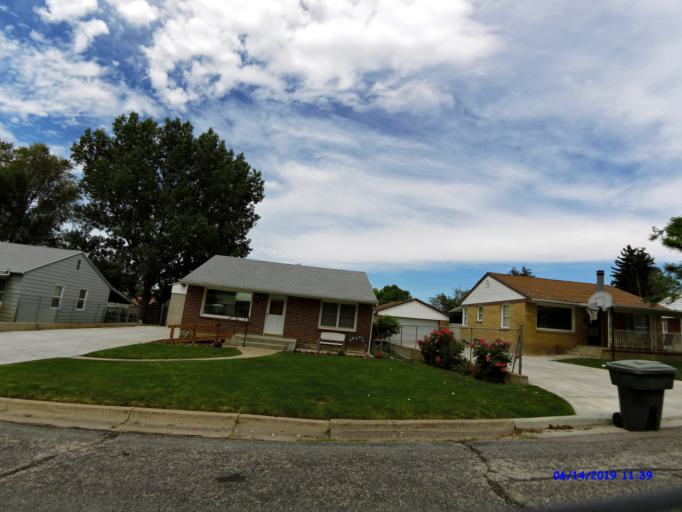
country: US
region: Utah
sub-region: Weber County
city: Ogden
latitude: 41.2506
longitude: -111.9410
